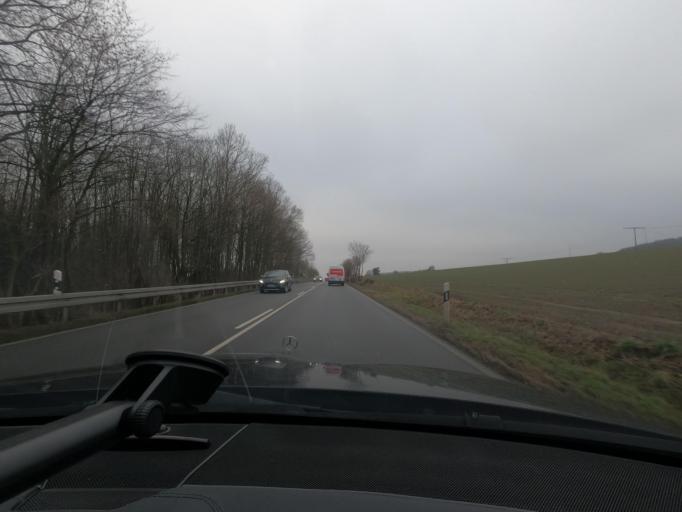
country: DE
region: Hesse
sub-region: Regierungsbezirk Kassel
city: Bad Arolsen
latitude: 51.4011
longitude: 9.0138
